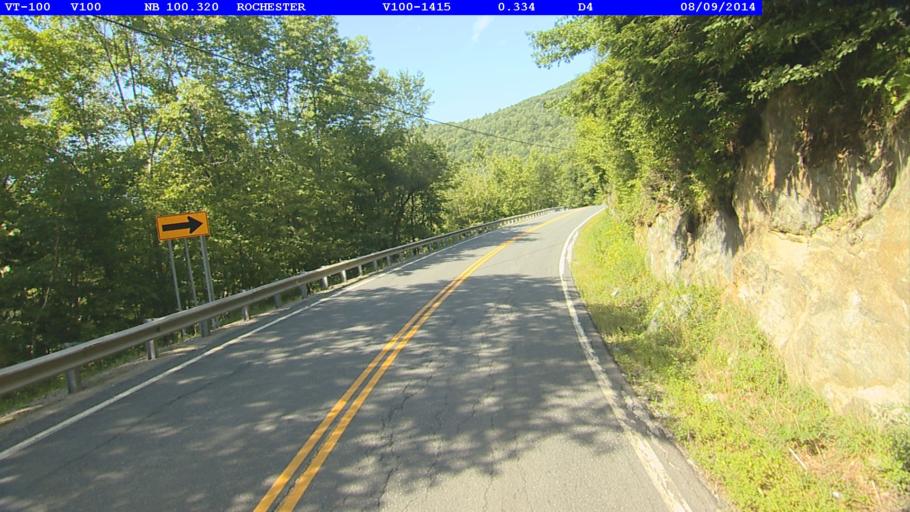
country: US
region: Vermont
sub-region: Orange County
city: Randolph
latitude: 43.8092
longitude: -72.7852
